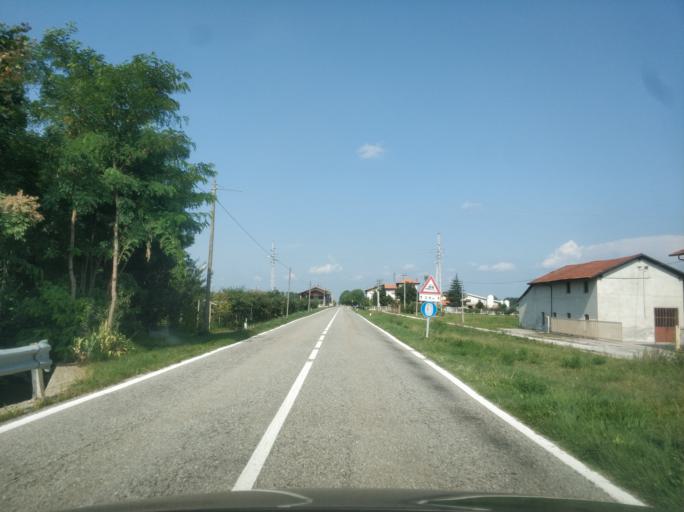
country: IT
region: Piedmont
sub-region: Provincia di Cuneo
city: Roata Rossi
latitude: 44.4583
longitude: 7.4913
